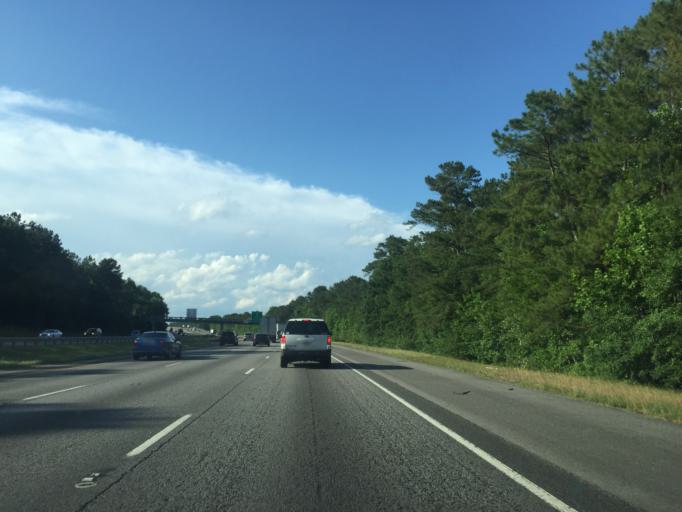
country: US
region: Georgia
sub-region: Chatham County
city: Pooler
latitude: 32.0931
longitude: -81.2367
